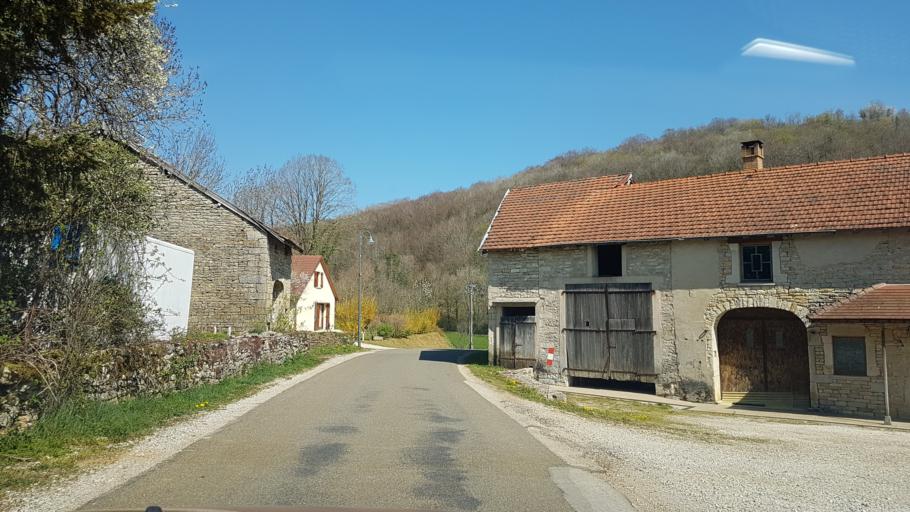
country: FR
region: Franche-Comte
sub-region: Departement du Jura
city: Orgelet
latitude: 46.5048
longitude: 5.5050
